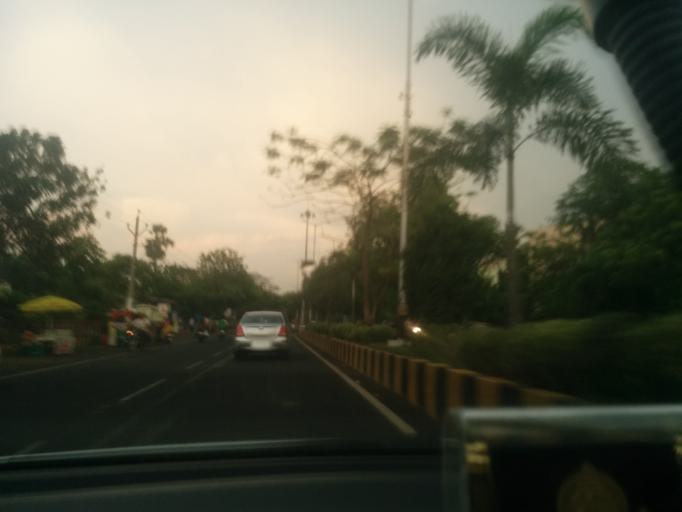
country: IN
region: Andhra Pradesh
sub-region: East Godavari
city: Rajahmundry
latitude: 17.0143
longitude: 81.7850
